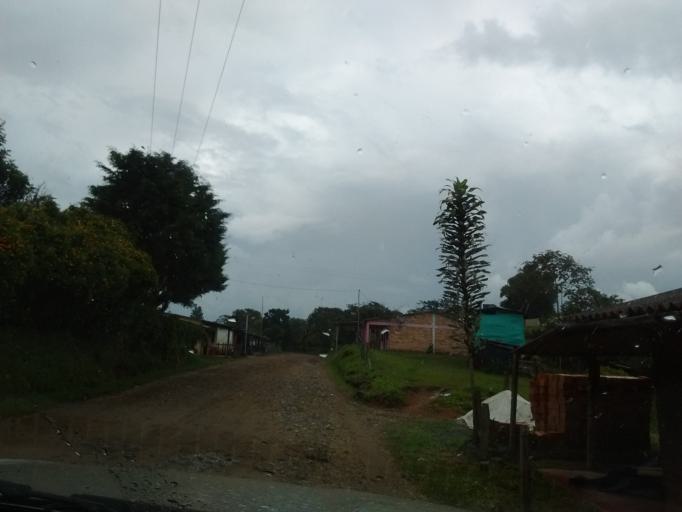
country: CO
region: Cauca
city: Cajibio
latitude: 2.5750
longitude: -76.6522
